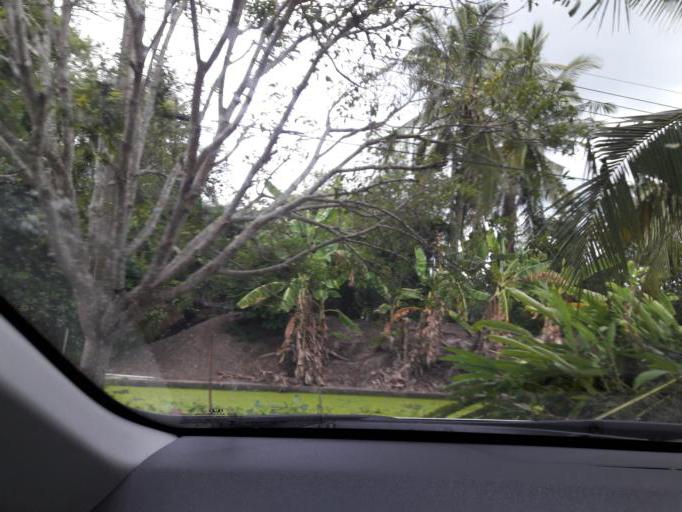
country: TH
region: Ratchaburi
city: Damnoen Saduak
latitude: 13.5462
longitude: 100.0007
